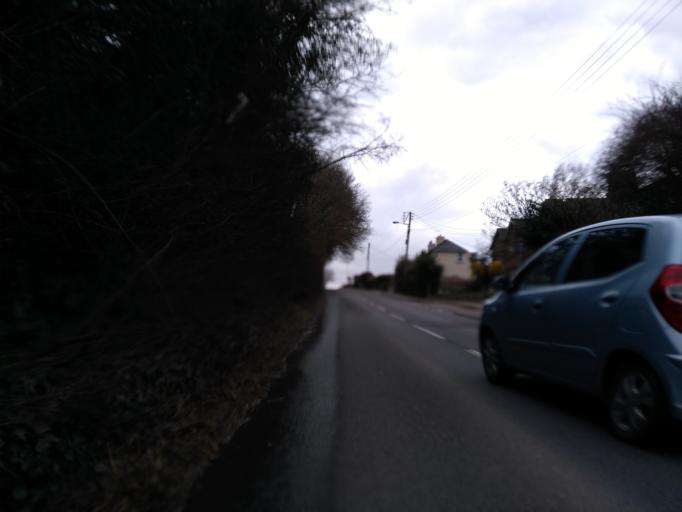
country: GB
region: England
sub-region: Devon
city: Exeter
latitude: 50.7552
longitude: -3.5544
